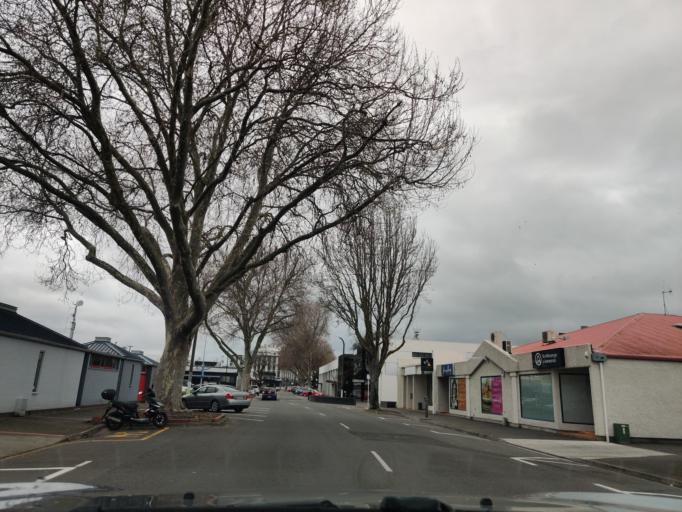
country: NZ
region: Hawke's Bay
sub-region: Napier City
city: Napier
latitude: -39.4931
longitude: 176.9147
